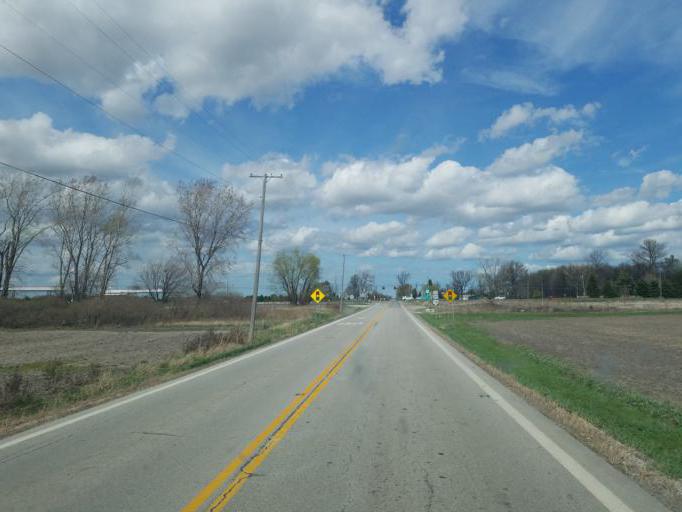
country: US
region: Ohio
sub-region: Huron County
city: Bellevue
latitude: 41.2633
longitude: -82.7957
